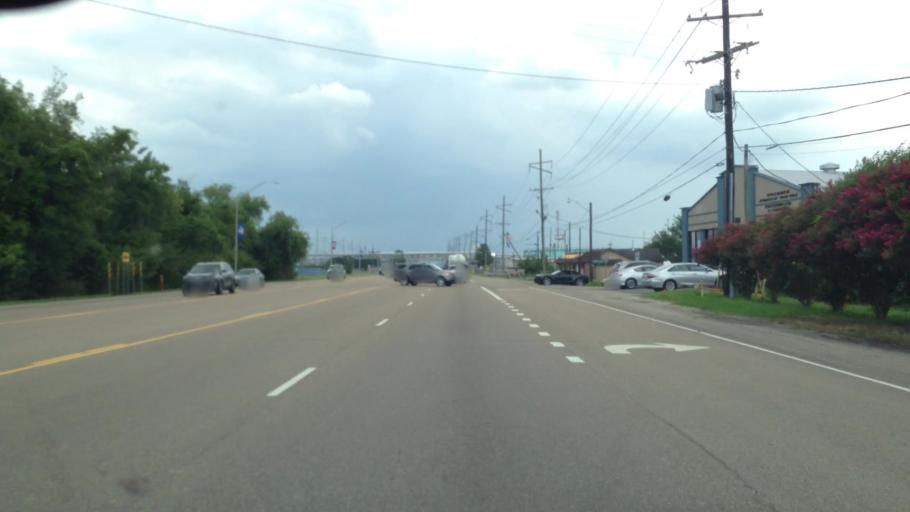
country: US
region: Louisiana
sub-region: Saint Charles Parish
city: Norco
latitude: 30.0150
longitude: -90.4065
